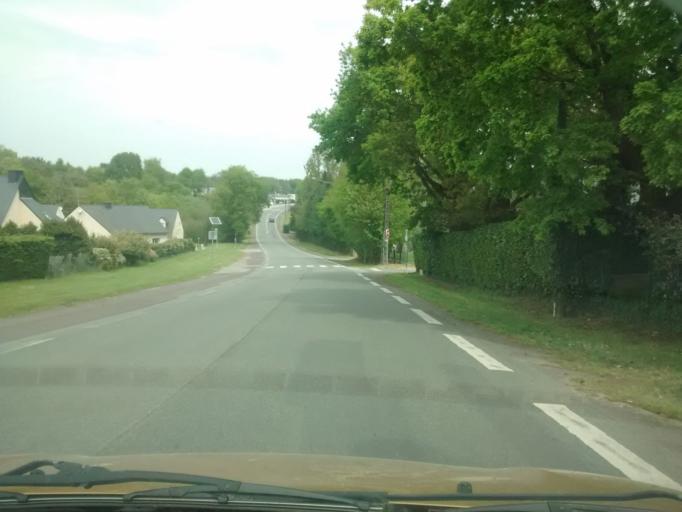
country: FR
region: Brittany
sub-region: Departement du Morbihan
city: Questembert
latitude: 47.6665
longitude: -2.4567
